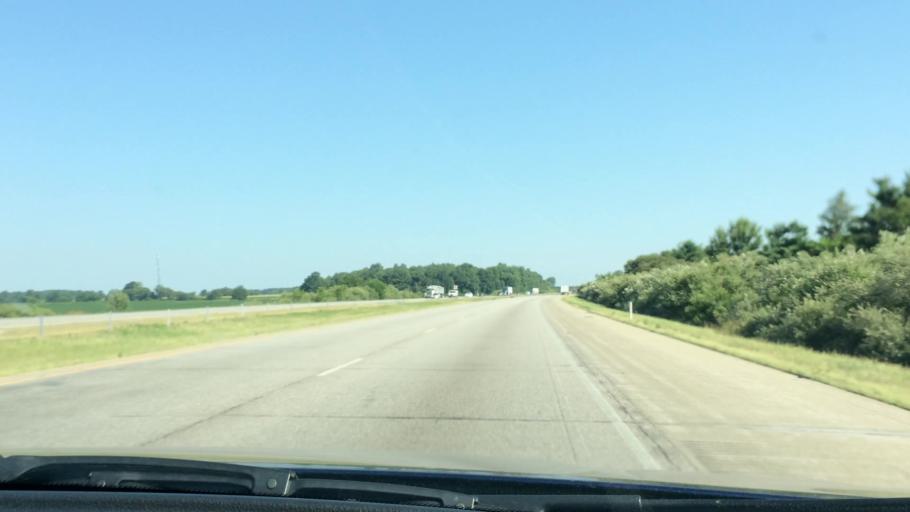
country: US
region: Indiana
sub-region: Jasper County
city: Rensselaer
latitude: 40.9770
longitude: -87.2509
